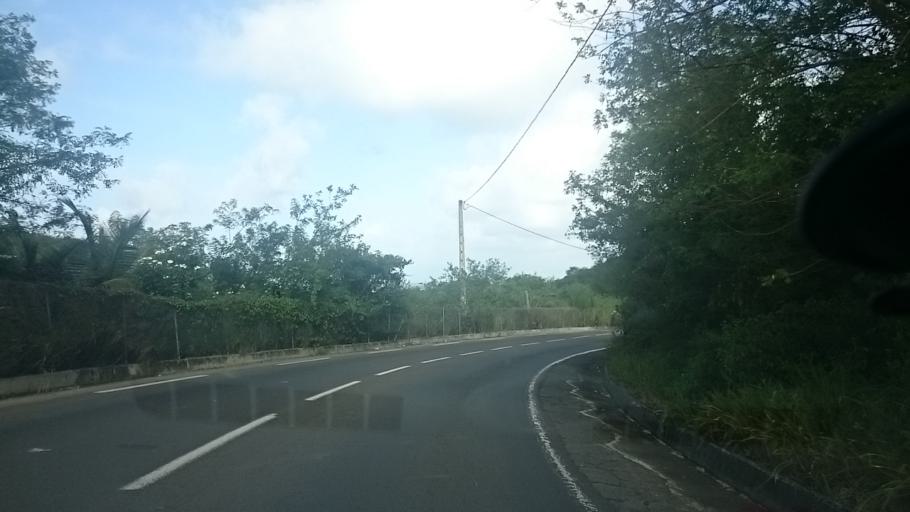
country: MQ
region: Martinique
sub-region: Martinique
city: Le Vauclin
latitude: 14.5620
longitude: -60.8528
